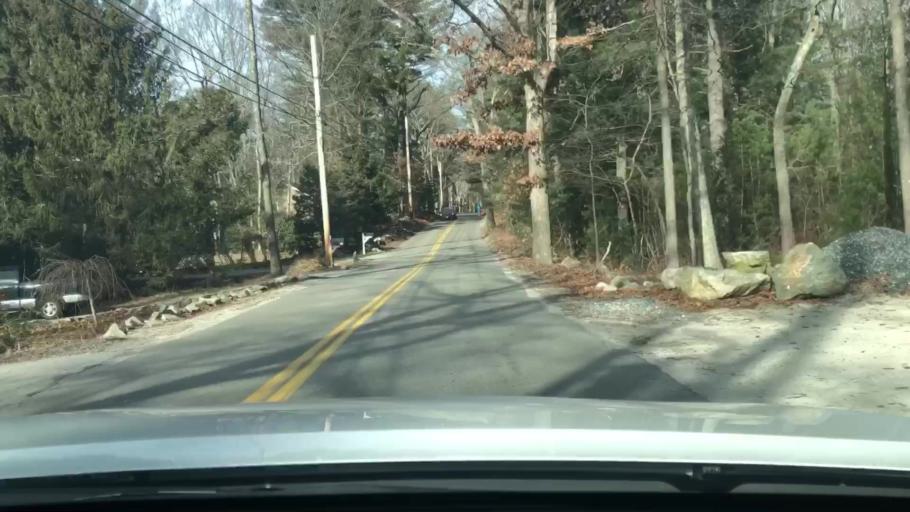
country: US
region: Massachusetts
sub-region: Norfolk County
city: Bellingham
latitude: 42.1066
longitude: -71.4960
